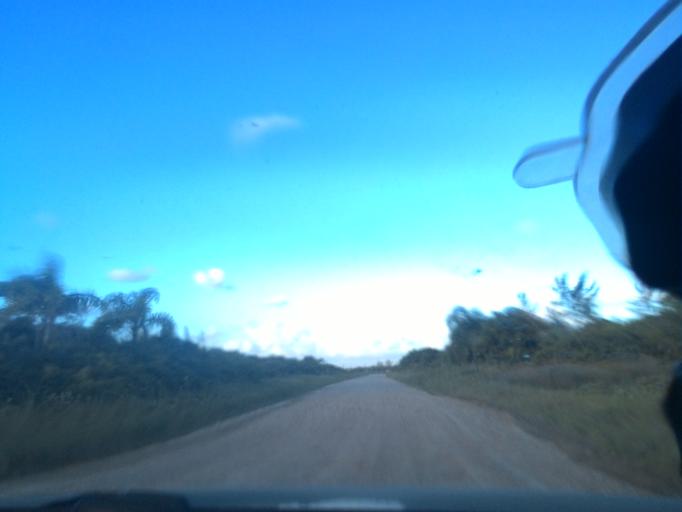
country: BR
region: Sao Paulo
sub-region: Iguape
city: Iguape
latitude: -24.8524
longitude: -47.7005
